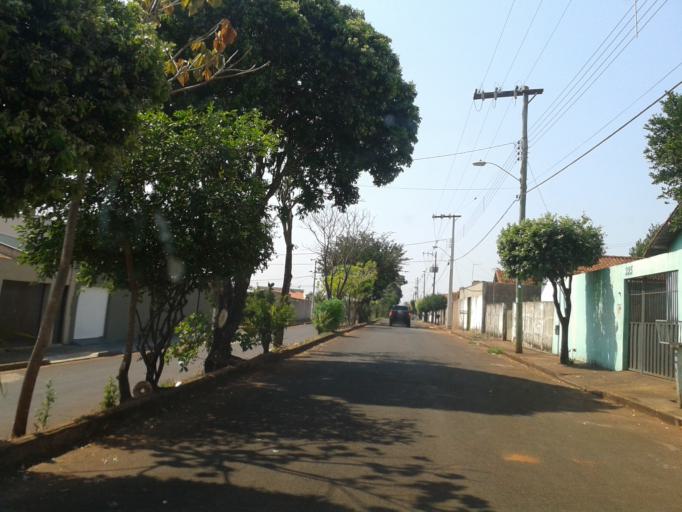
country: BR
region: Minas Gerais
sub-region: Ituiutaba
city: Ituiutaba
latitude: -18.9755
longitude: -49.4871
